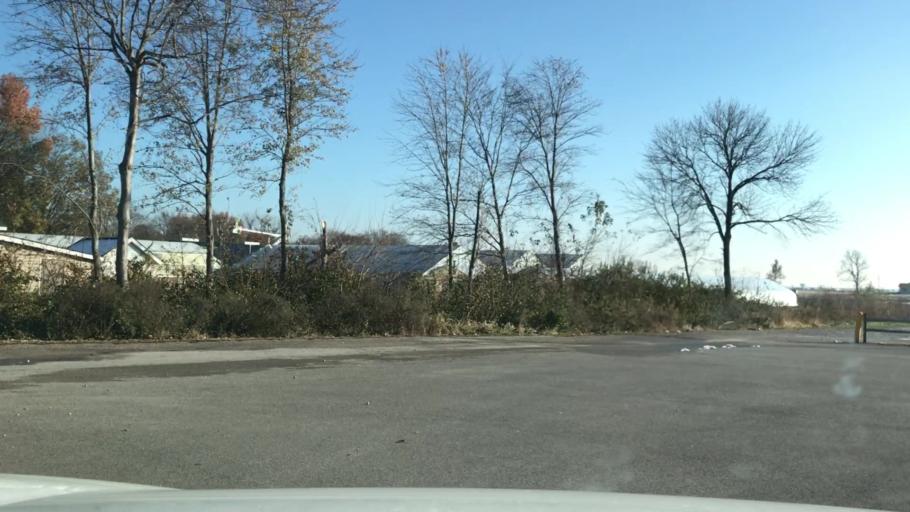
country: US
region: Illinois
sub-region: Clinton County
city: New Baden
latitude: 38.5349
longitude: -89.7074
